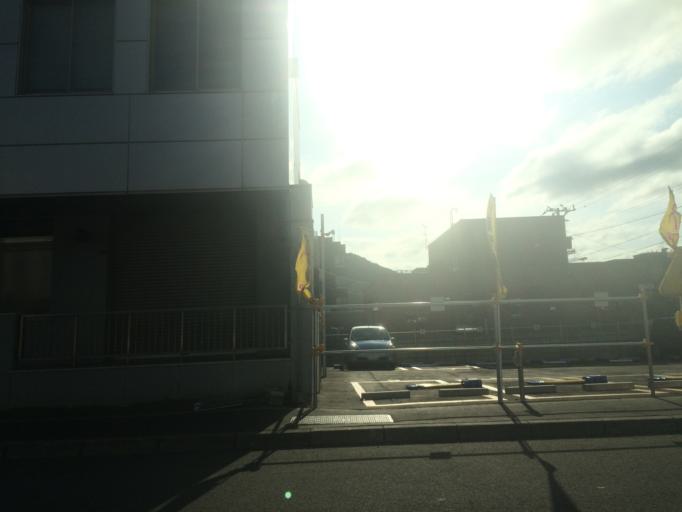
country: JP
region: Hokkaido
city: Sapporo
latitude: 43.0311
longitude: 141.3448
